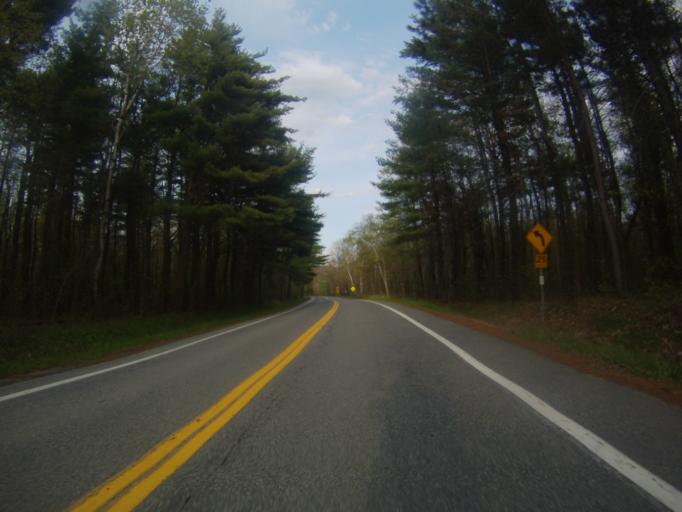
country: US
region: New York
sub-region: Essex County
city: Ticonderoga
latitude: 43.7505
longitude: -73.5665
